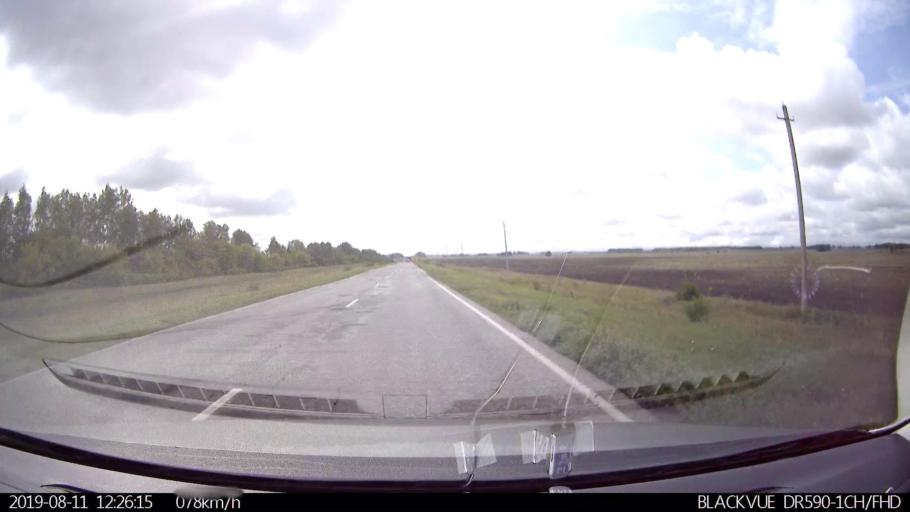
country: RU
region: Ulyanovsk
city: Ignatovka
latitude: 53.8659
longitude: 47.9323
